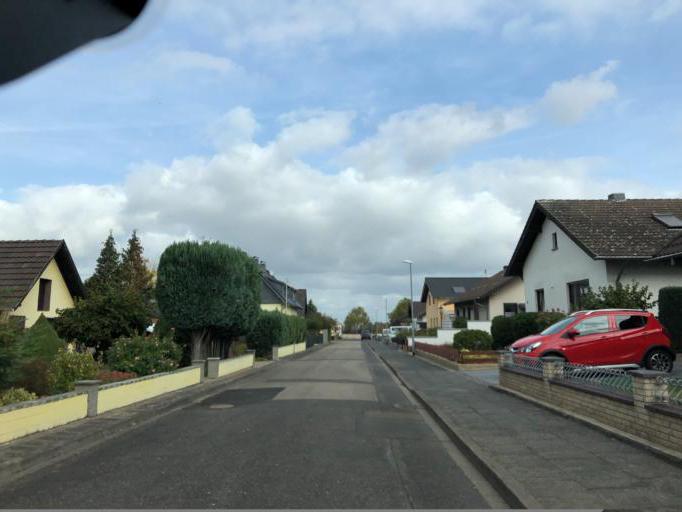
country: DE
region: North Rhine-Westphalia
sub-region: Regierungsbezirk Koln
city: Rheinbach
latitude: 50.6383
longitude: 6.9235
